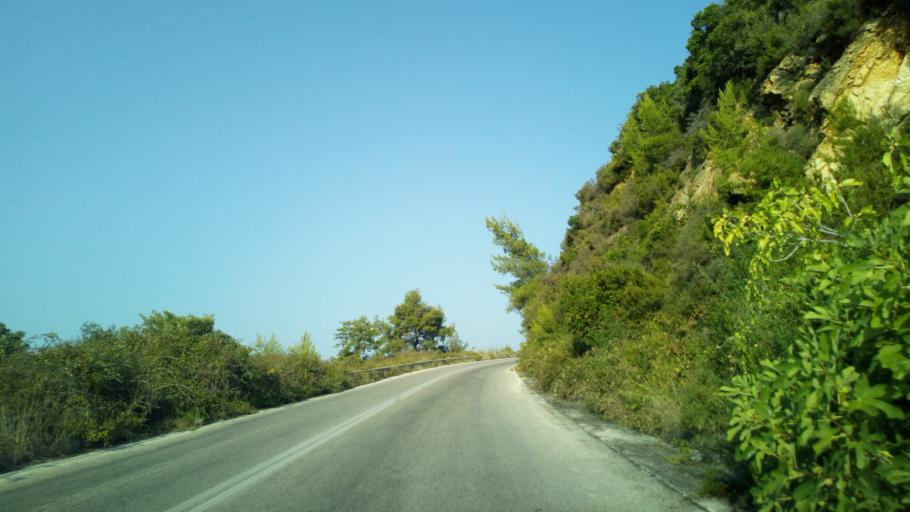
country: GR
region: Central Macedonia
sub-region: Nomos Chalkidikis
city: Neos Marmaras
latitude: 40.1728
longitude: 23.8558
